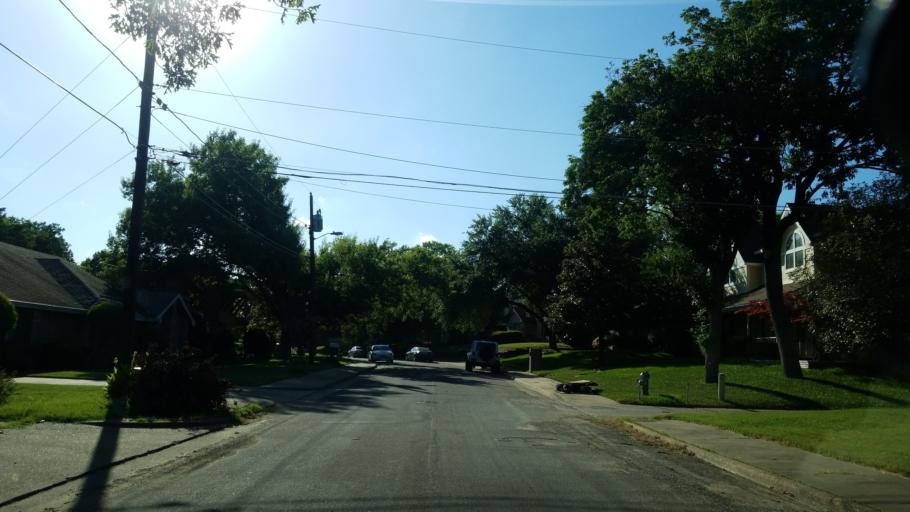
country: US
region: Texas
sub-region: Dallas County
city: Balch Springs
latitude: 32.7805
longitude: -96.7068
